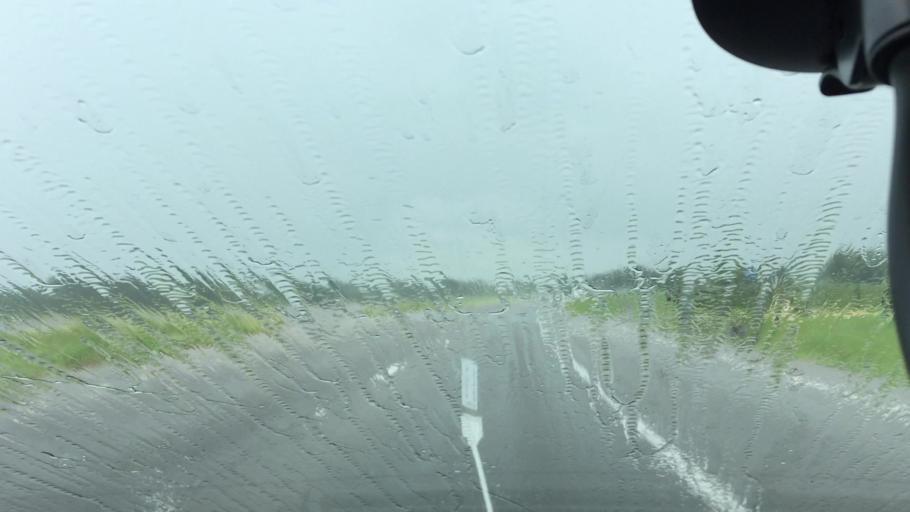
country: US
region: Alabama
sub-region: Montgomery County
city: Pike Road
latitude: 32.2298
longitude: -86.1207
